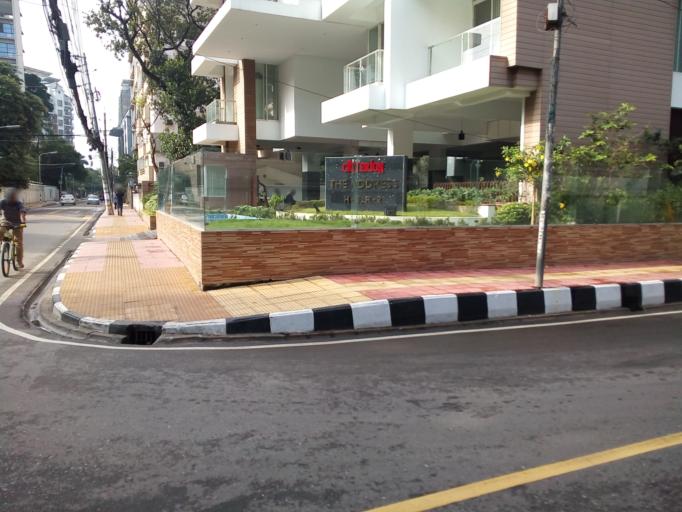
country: BD
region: Dhaka
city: Paltan
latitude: 23.7773
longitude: 90.4153
